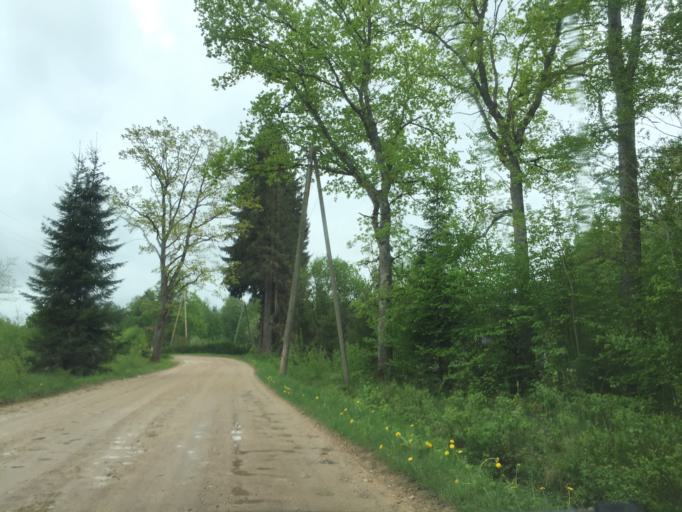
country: LV
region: Lielvarde
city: Lielvarde
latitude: 56.7283
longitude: 24.7871
